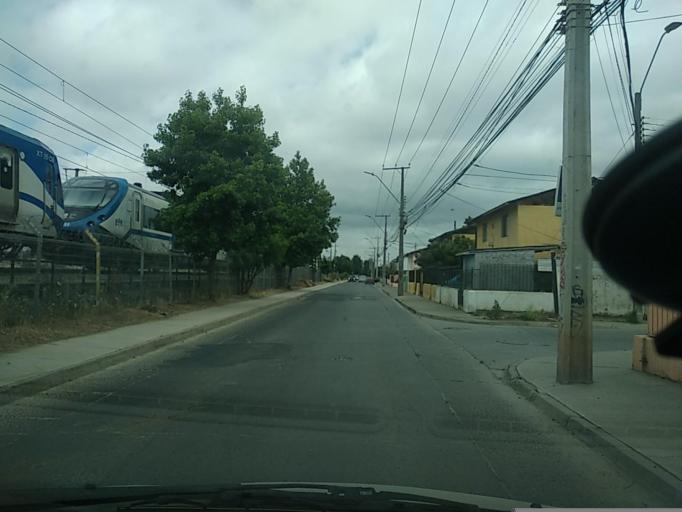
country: CL
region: Valparaiso
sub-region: Provincia de Marga Marga
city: Villa Alemana
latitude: -33.0417
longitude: -71.3631
